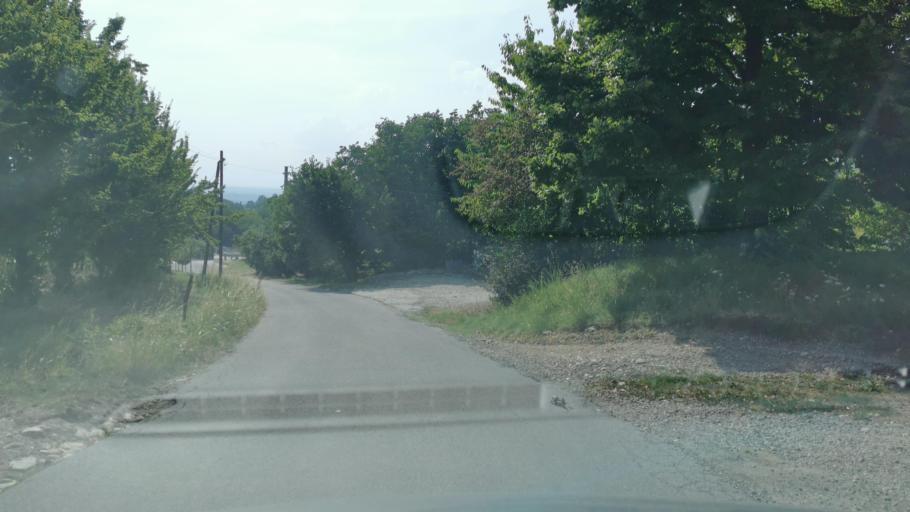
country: IT
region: Piedmont
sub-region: Provincia di Cuneo
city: La Morra
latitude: 44.6441
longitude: 7.9278
